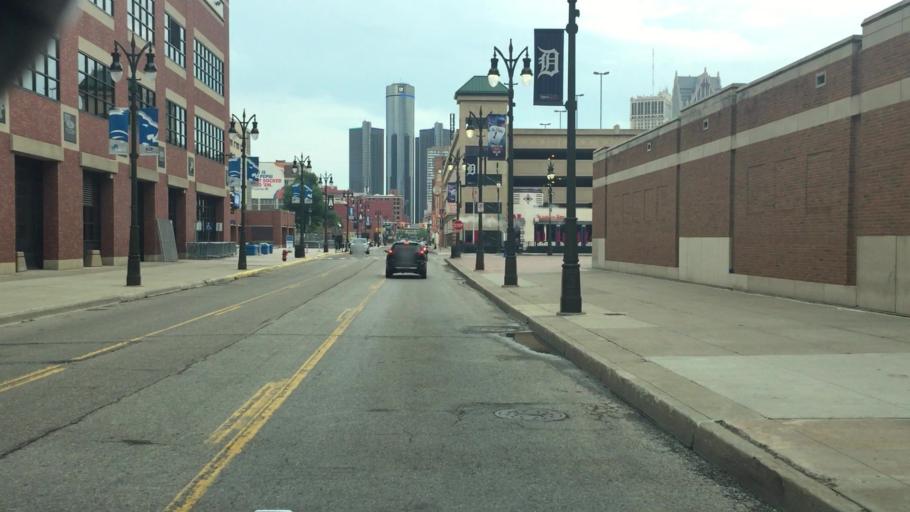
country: US
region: Michigan
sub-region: Wayne County
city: Detroit
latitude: 42.3395
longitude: -83.0471
